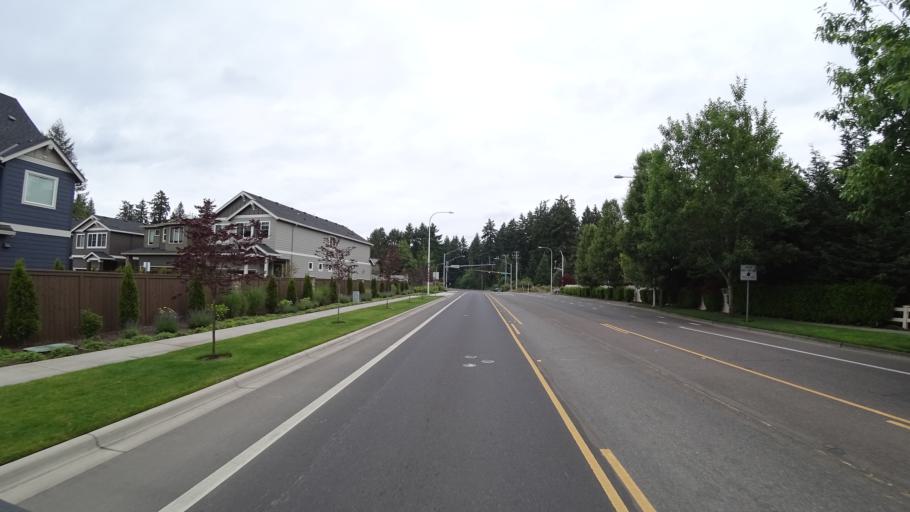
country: US
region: Oregon
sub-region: Washington County
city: Hillsboro
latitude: 45.4930
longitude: -122.9400
